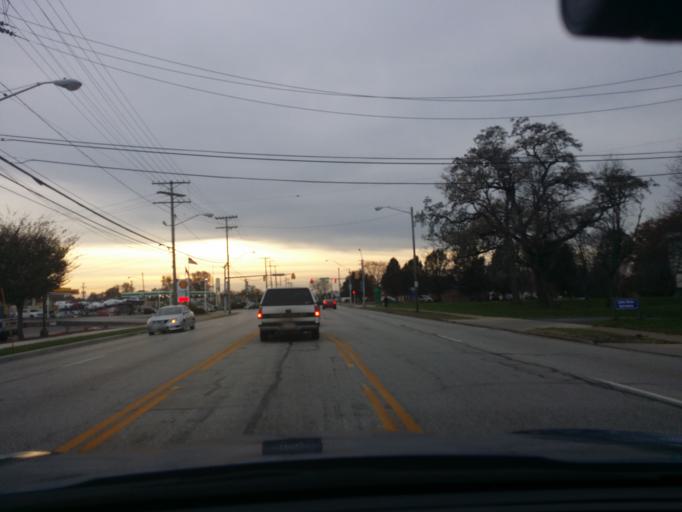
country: US
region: Ohio
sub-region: Cuyahoga County
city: North Olmsted
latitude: 41.4244
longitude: -81.9004
